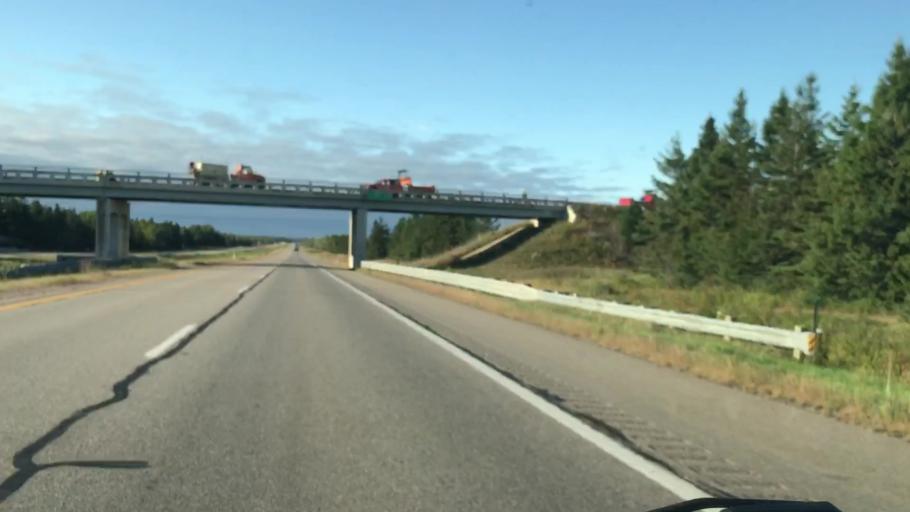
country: US
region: Michigan
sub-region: Chippewa County
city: Sault Ste. Marie
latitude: 46.4200
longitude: -84.3952
